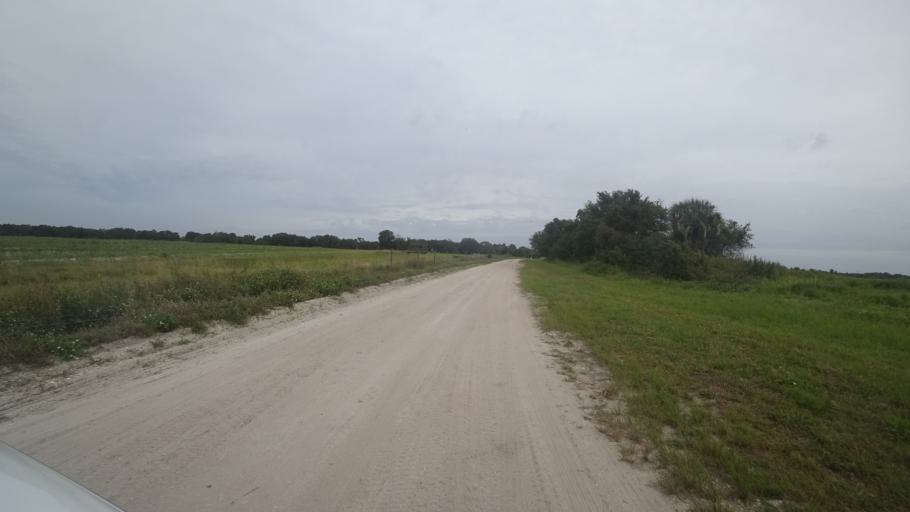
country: US
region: Florida
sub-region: Hillsborough County
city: Wimauma
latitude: 27.5938
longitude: -82.2864
